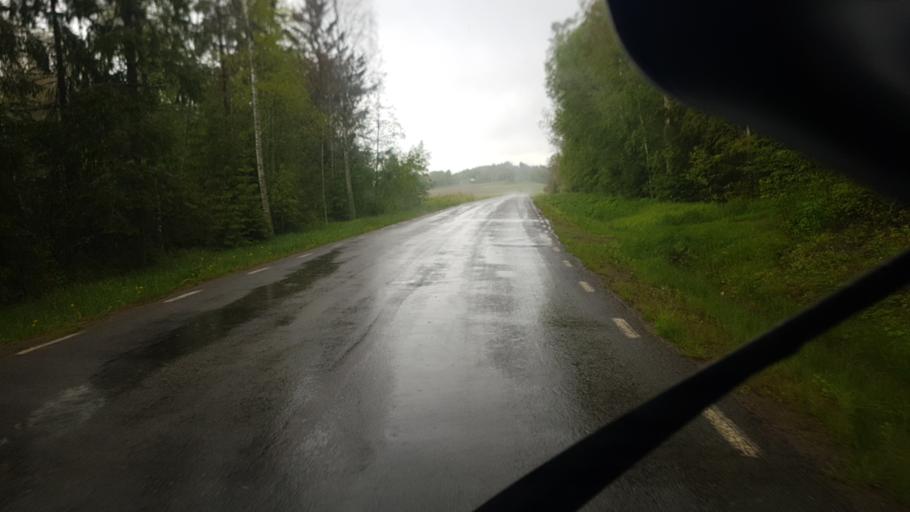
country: SE
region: Vaermland
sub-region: Eda Kommun
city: Amotfors
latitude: 59.7047
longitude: 12.4525
